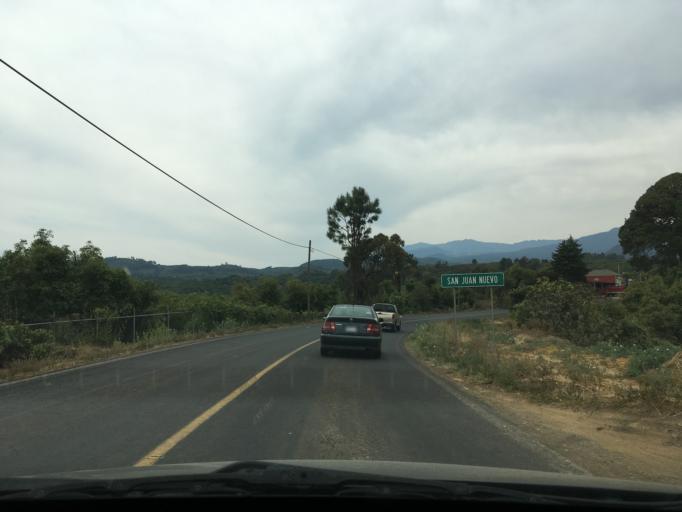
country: MX
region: Michoacan
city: Nuevo San Juan Parangaricutiro
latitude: 19.4056
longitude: -102.1113
